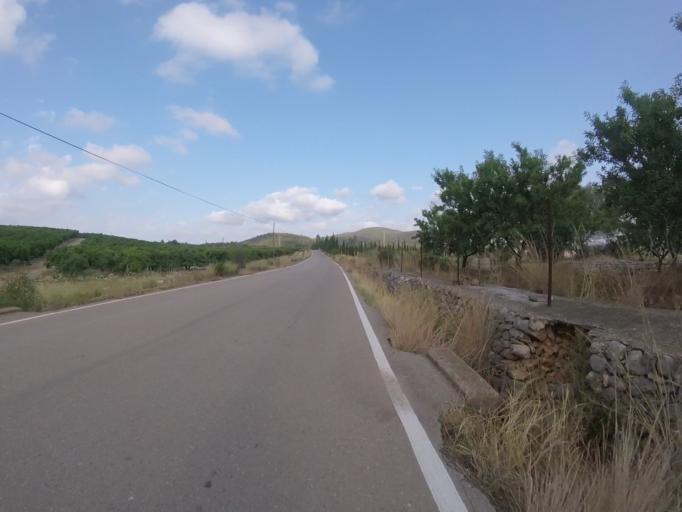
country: ES
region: Valencia
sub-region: Provincia de Castello
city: Santa Magdalena de Pulpis
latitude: 40.3603
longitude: 0.2886
